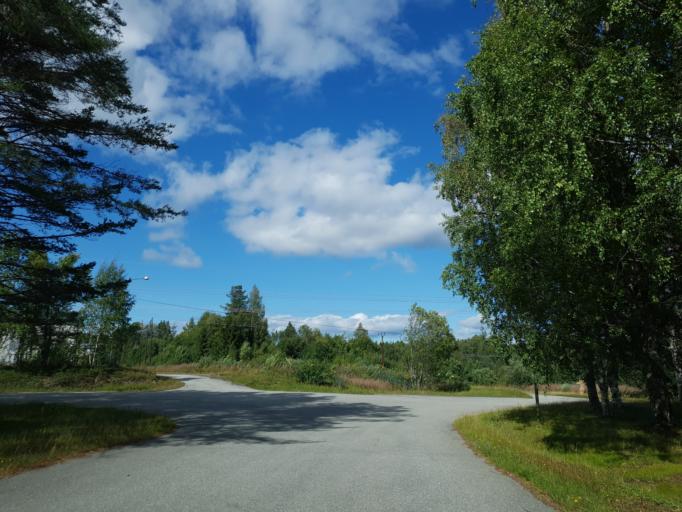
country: SE
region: Vaesternorrland
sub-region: OErnskoeldsviks Kommun
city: Husum
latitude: 63.3444
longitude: 19.1138
